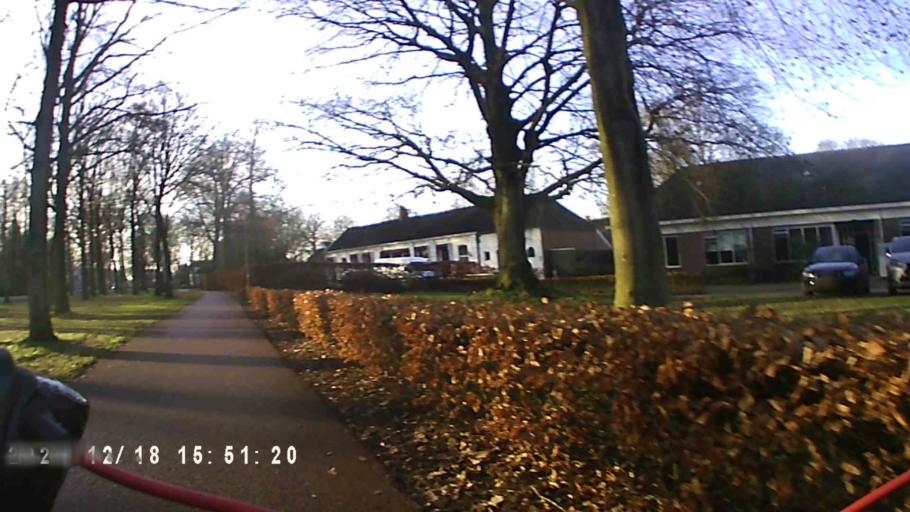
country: NL
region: Drenthe
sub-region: Gemeente Tynaarlo
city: Zuidlaren
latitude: 53.0974
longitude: 6.6905
